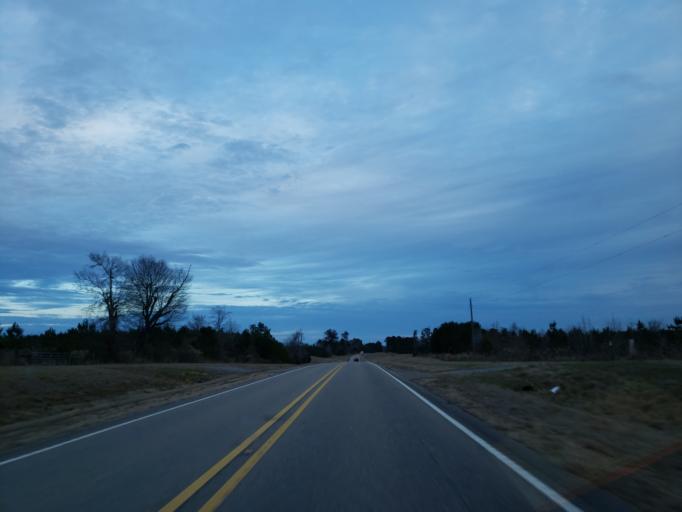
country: US
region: Mississippi
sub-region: Kemper County
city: De Kalb
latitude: 32.8308
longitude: -88.3716
